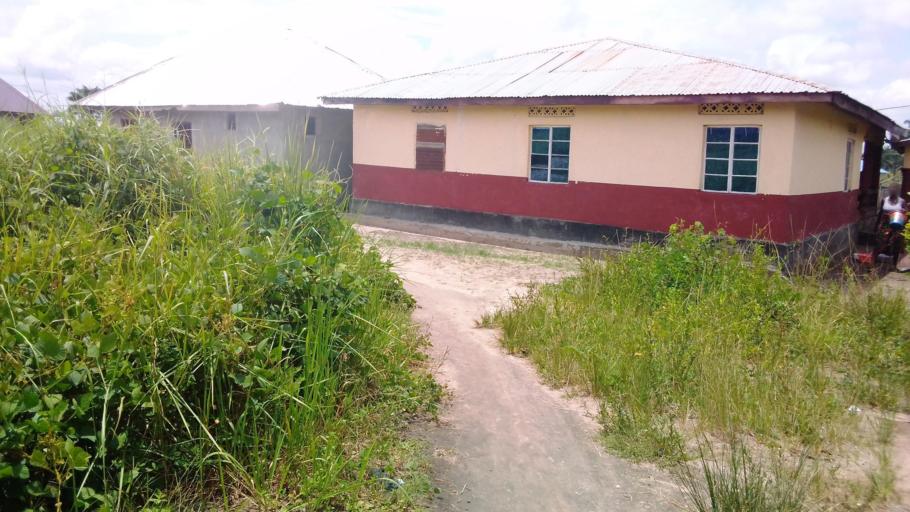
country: SL
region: Northern Province
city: Makeni
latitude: 8.8629
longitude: -12.0398
